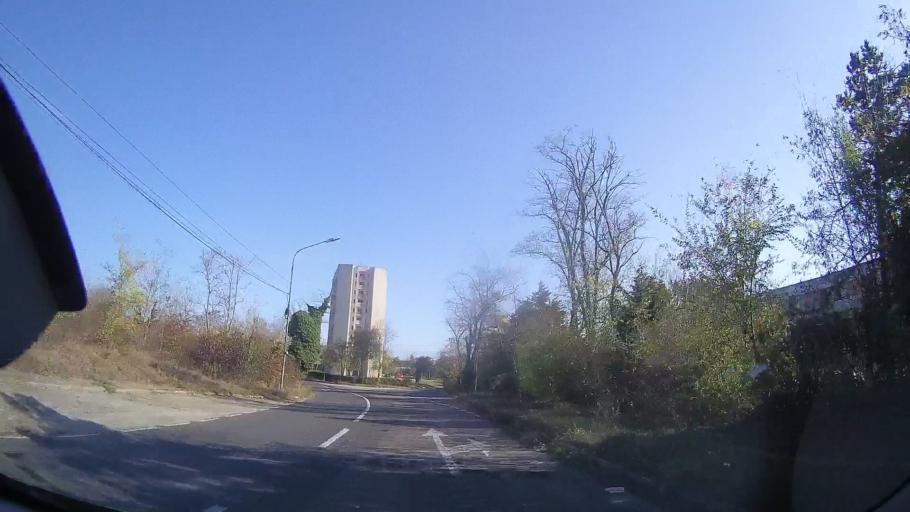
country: RO
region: Constanta
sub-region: Municipiul Mangalia
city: Mangalia
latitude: 43.8477
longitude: 28.5945
